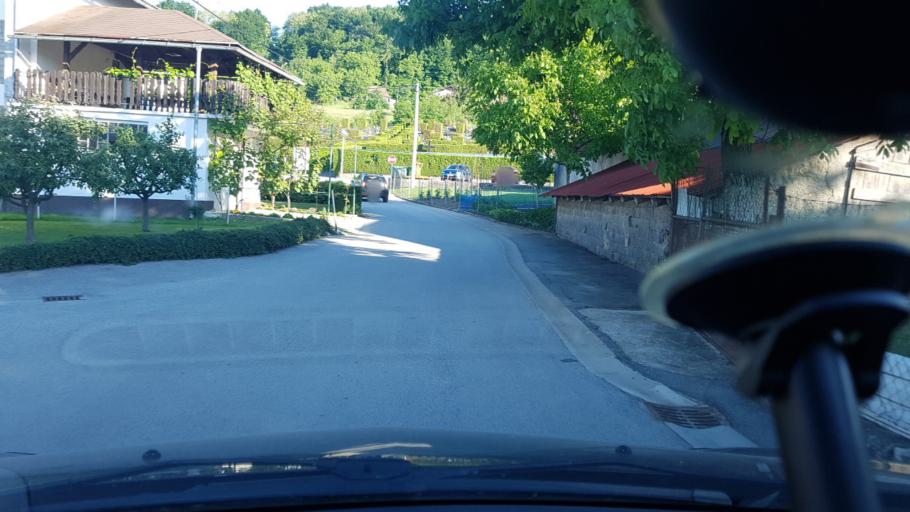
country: HR
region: Krapinsko-Zagorska
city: Radoboj
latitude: 46.2070
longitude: 15.9087
